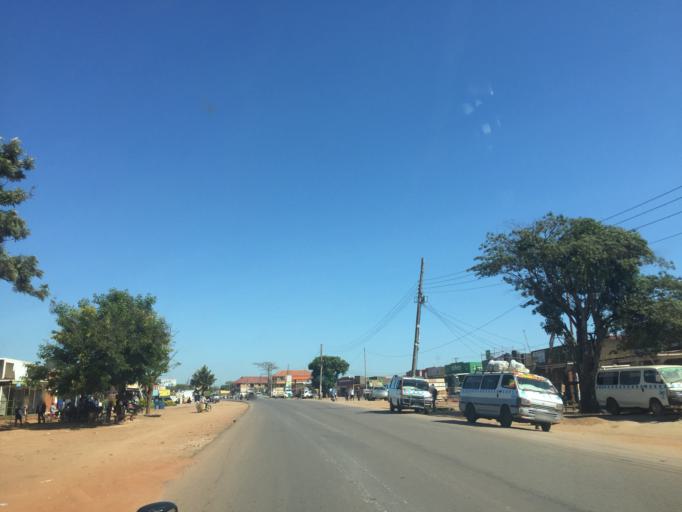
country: UG
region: Central Region
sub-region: Luwero District
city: Luwero
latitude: 0.8290
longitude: 32.5015
